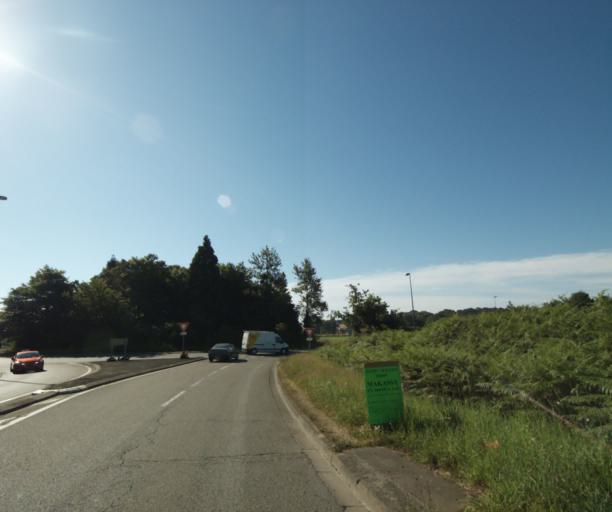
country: FR
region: Pays de la Loire
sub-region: Departement de la Mayenne
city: Laval
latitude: 48.0502
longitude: -0.7355
